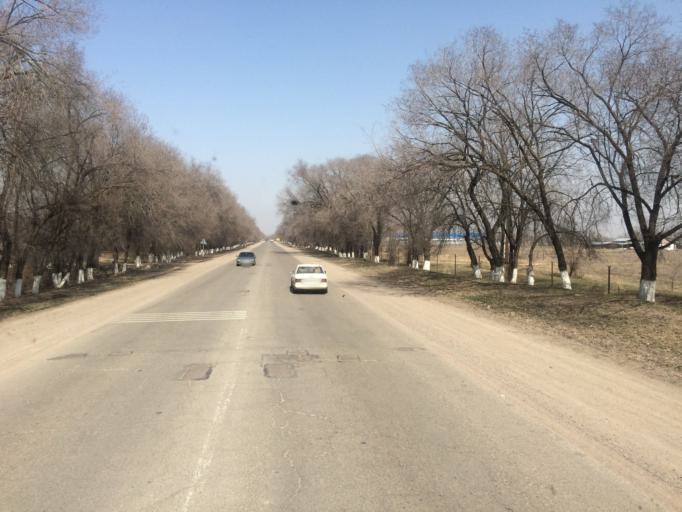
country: KZ
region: Almaty Oblysy
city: Burunday
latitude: 43.2312
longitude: 76.6630
